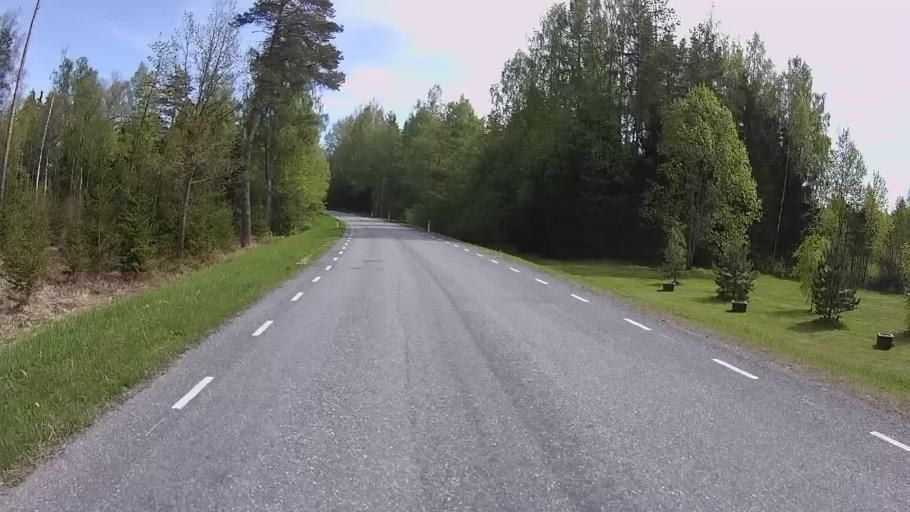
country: EE
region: Valgamaa
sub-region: Valga linn
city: Valga
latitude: 57.6964
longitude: 26.2527
